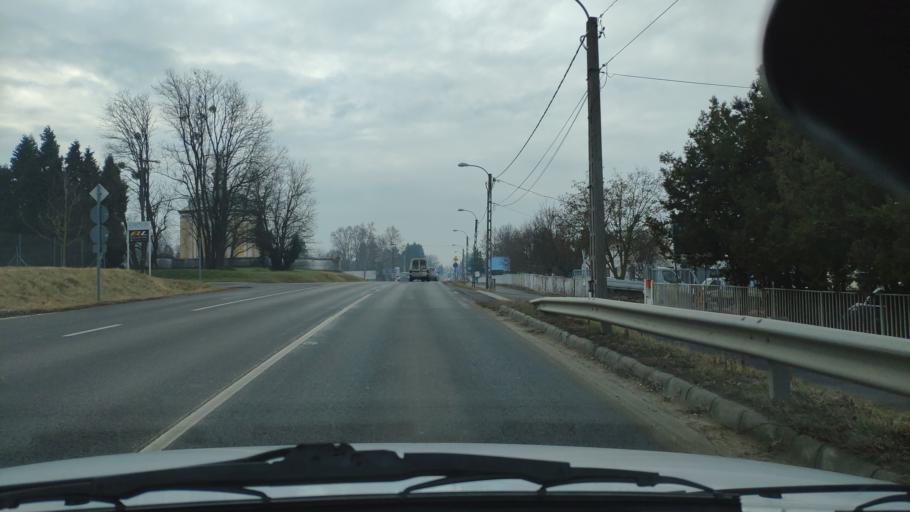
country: HU
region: Zala
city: Nagykanizsa
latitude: 46.4749
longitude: 16.9858
